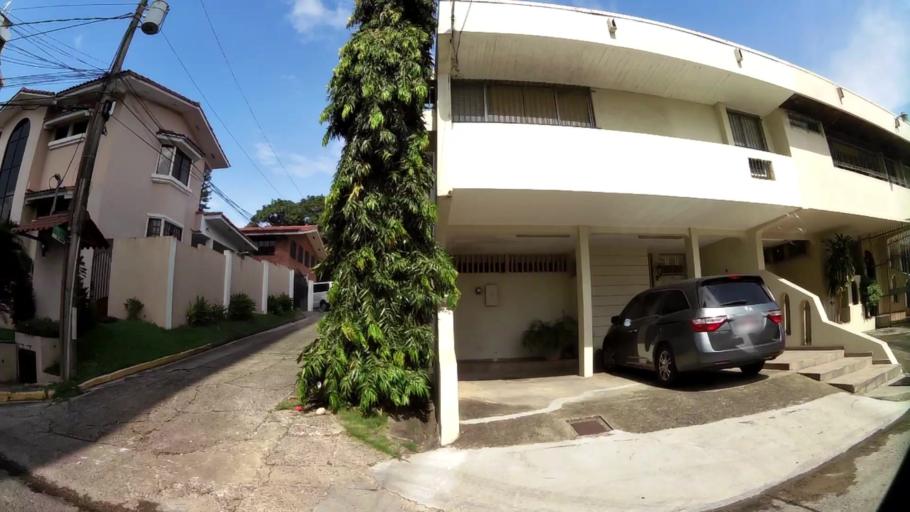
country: PA
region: Panama
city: Panama
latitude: 8.9978
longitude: -79.5238
